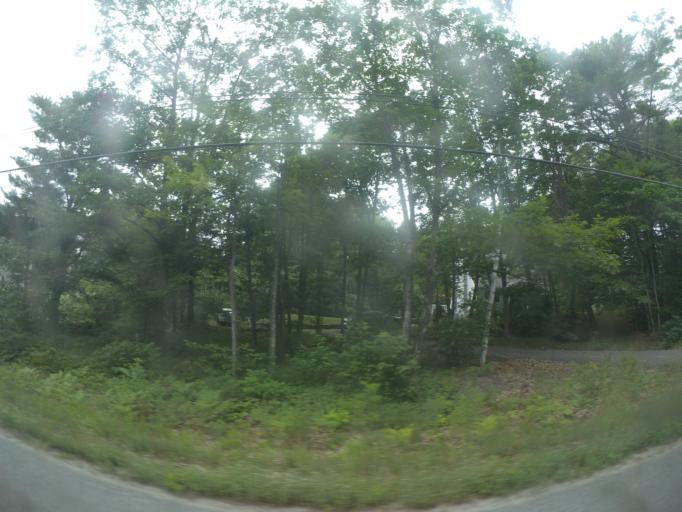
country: US
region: Maine
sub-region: Cumberland County
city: Falmouth
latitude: 43.7423
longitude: -70.2393
